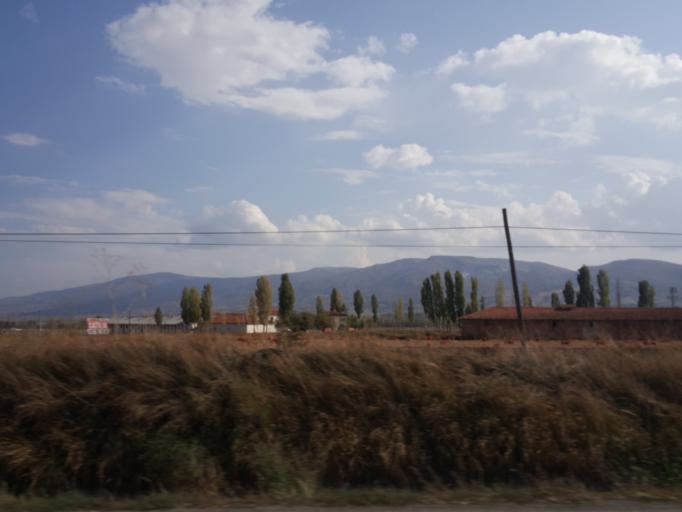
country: TR
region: Corum
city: Seydim
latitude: 40.4398
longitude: 34.8156
